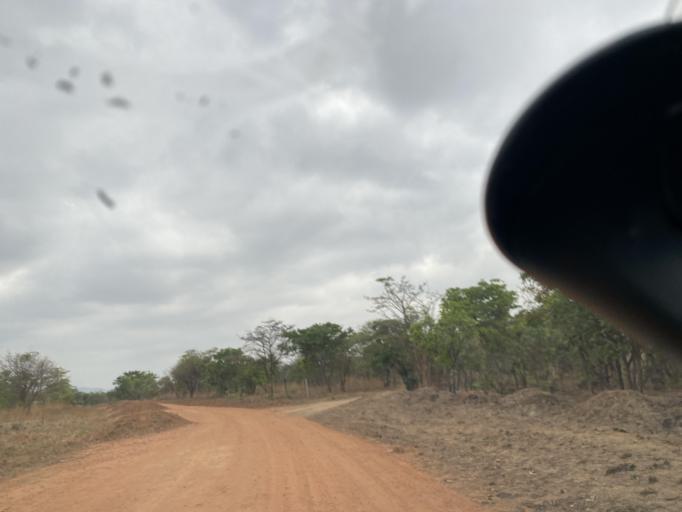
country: ZM
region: Lusaka
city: Chongwe
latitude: -15.2234
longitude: 28.7502
